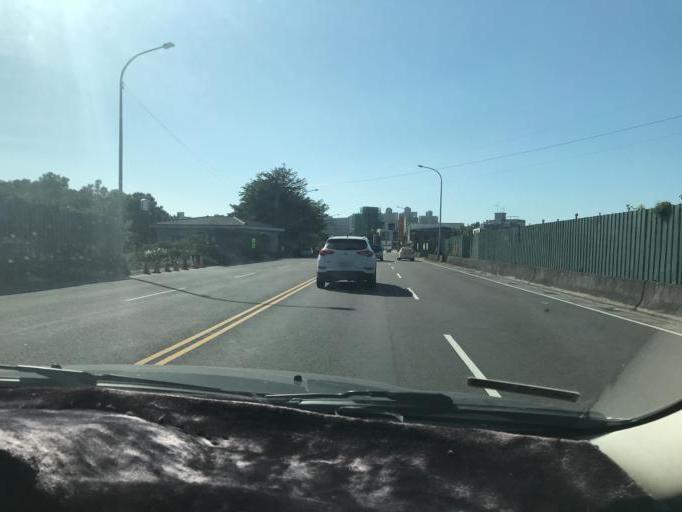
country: TW
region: Taiwan
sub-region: Hsinchu
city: Hsinchu
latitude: 24.8172
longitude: 120.9867
